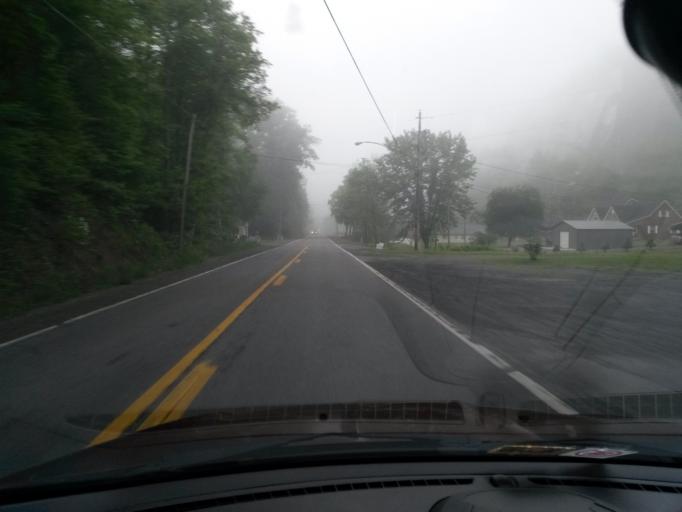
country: US
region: West Virginia
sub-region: McDowell County
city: Welch
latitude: 37.4704
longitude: -81.5417
